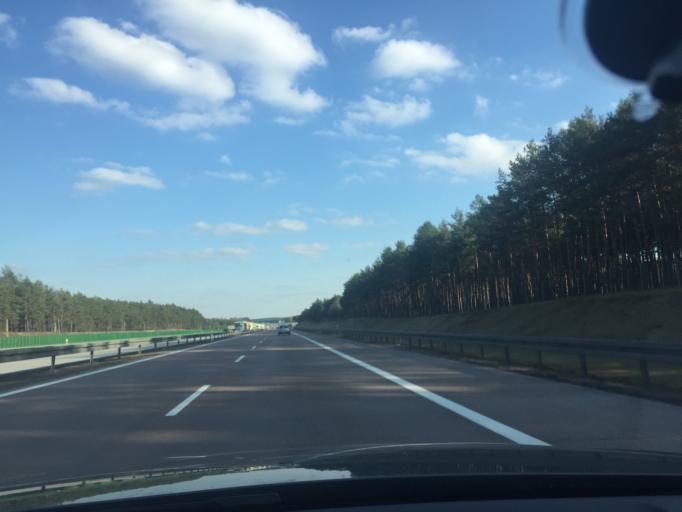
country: PL
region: Lubusz
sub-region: Powiat slubicki
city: Rzepin
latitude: 52.3336
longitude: 14.8121
